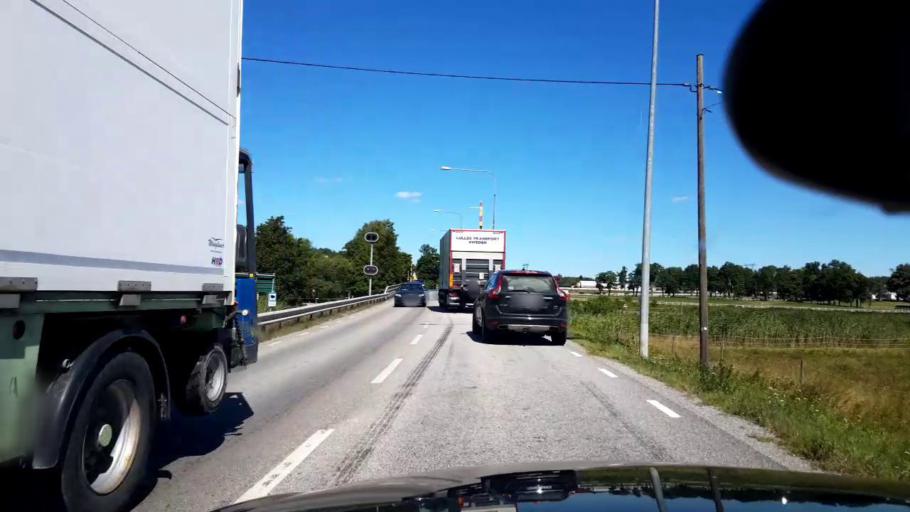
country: SE
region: Uppsala
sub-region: Habo Kommun
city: Balsta
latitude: 59.6395
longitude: 17.6093
